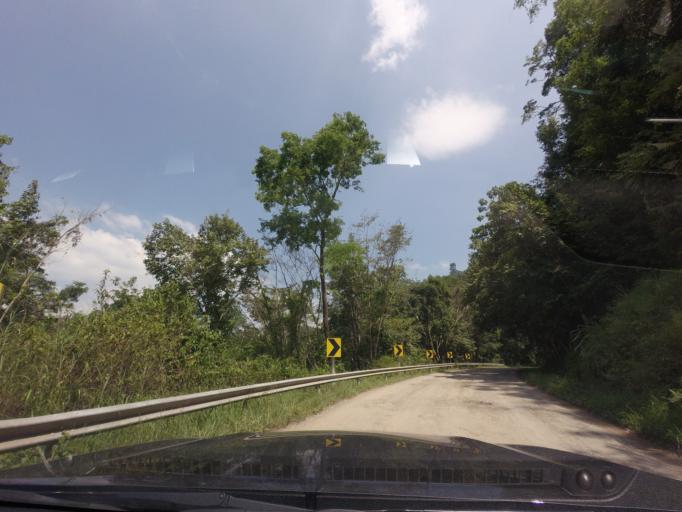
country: TH
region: Loei
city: Na Haeo
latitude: 17.6158
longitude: 100.8972
